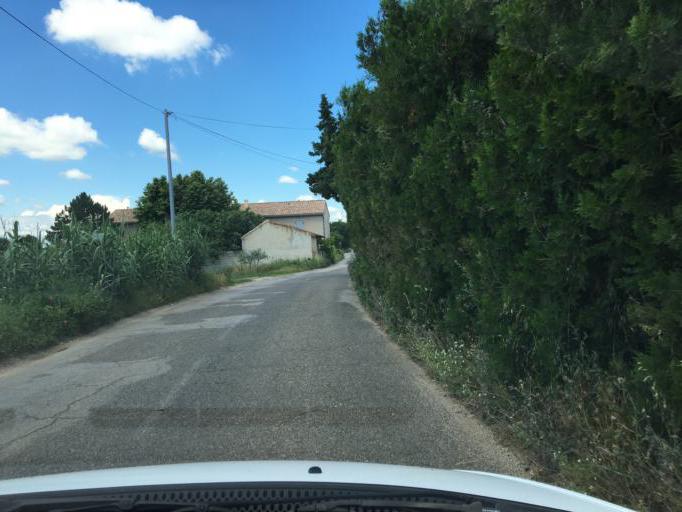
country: FR
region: Provence-Alpes-Cote d'Azur
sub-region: Departement du Vaucluse
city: Carpentras
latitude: 44.0376
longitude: 5.0565
